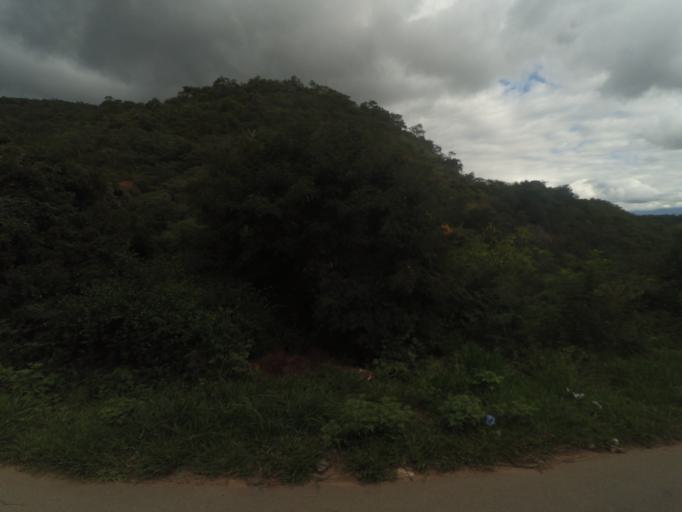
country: BO
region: Santa Cruz
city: Samaipata
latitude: -18.1664
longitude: -63.9074
